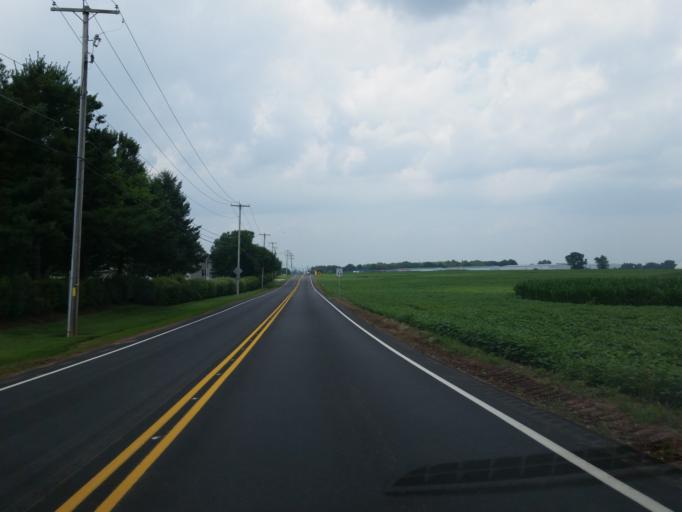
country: US
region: Pennsylvania
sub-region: Lebanon County
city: Campbelltown
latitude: 40.2808
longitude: -76.5723
